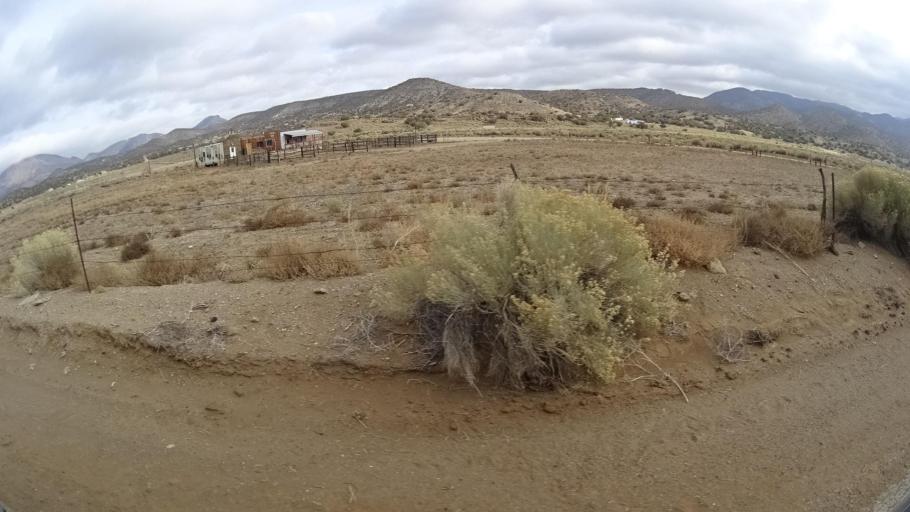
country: US
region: California
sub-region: Kern County
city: Tehachapi
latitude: 35.1609
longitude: -118.3259
